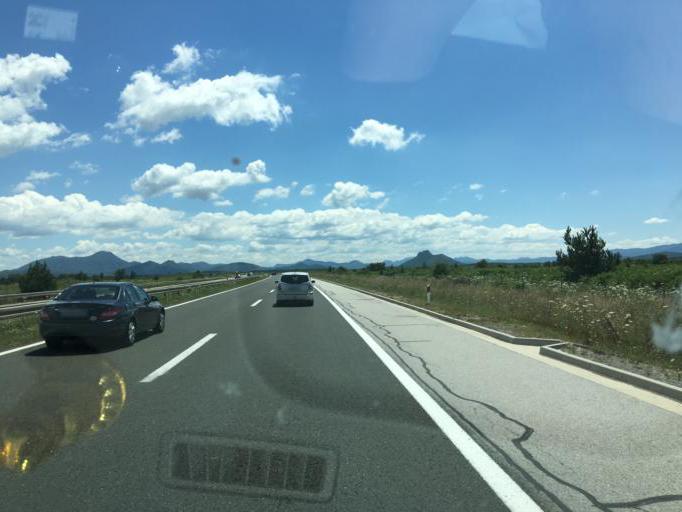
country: HR
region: Licko-Senjska
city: Gospic
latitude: 44.4852
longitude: 15.5493
